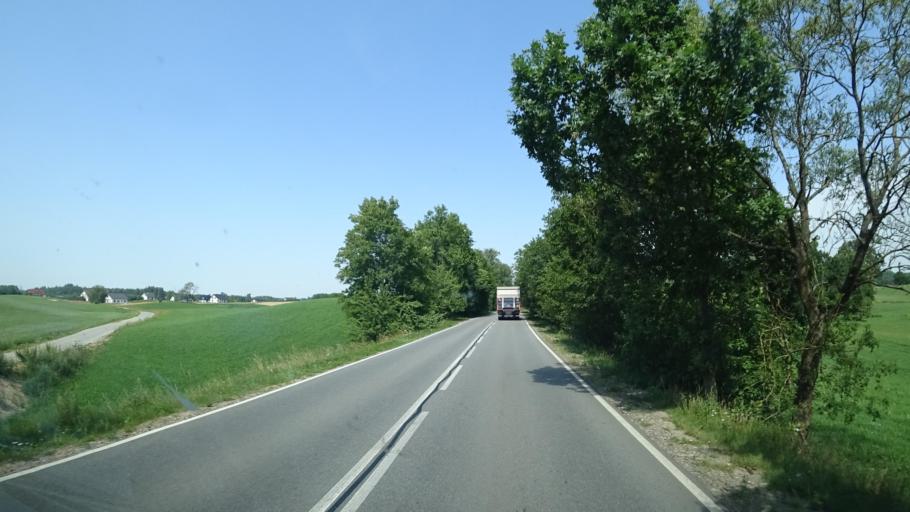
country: PL
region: Pomeranian Voivodeship
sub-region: Powiat koscierski
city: Lipusz
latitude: 54.0785
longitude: 17.7983
